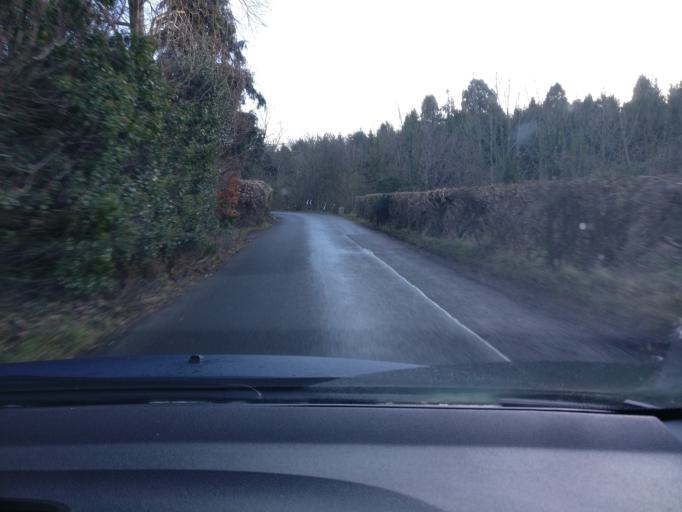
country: GB
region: Scotland
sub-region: The Scottish Borders
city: Hawick
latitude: 55.4431
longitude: -2.7417
